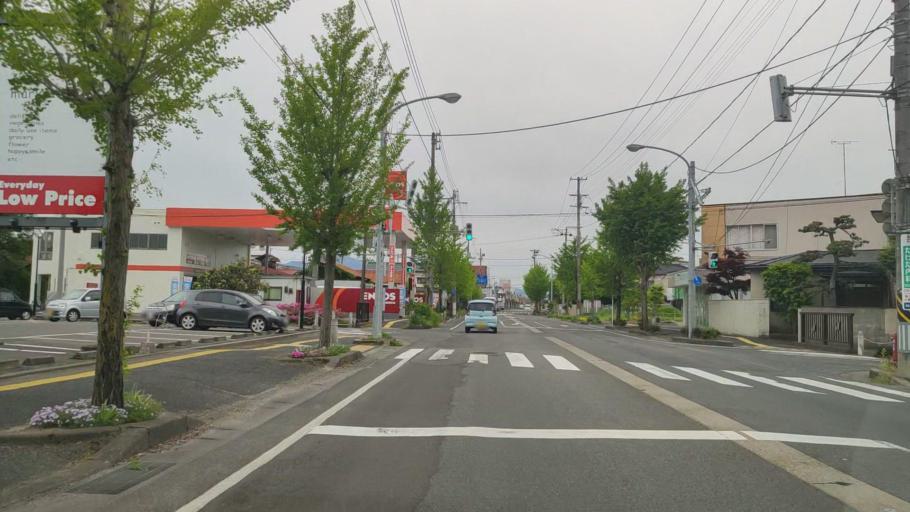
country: JP
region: Niigata
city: Gosen
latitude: 37.7394
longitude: 139.1807
